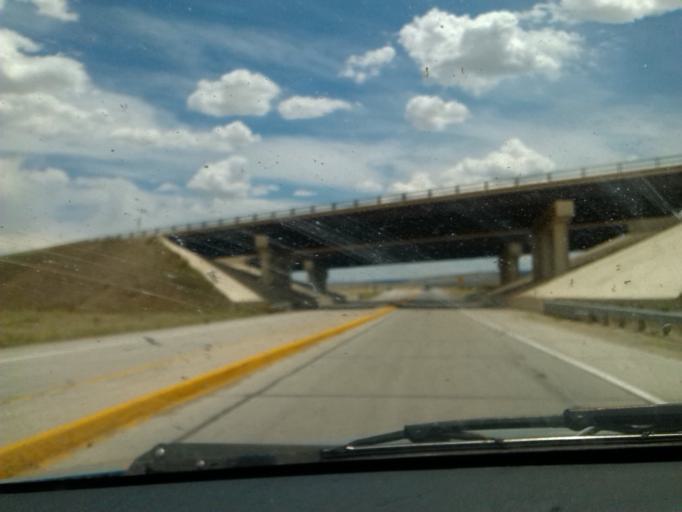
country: US
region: Wyoming
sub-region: Carbon County
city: Rawlins
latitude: 41.7894
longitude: -107.2010
